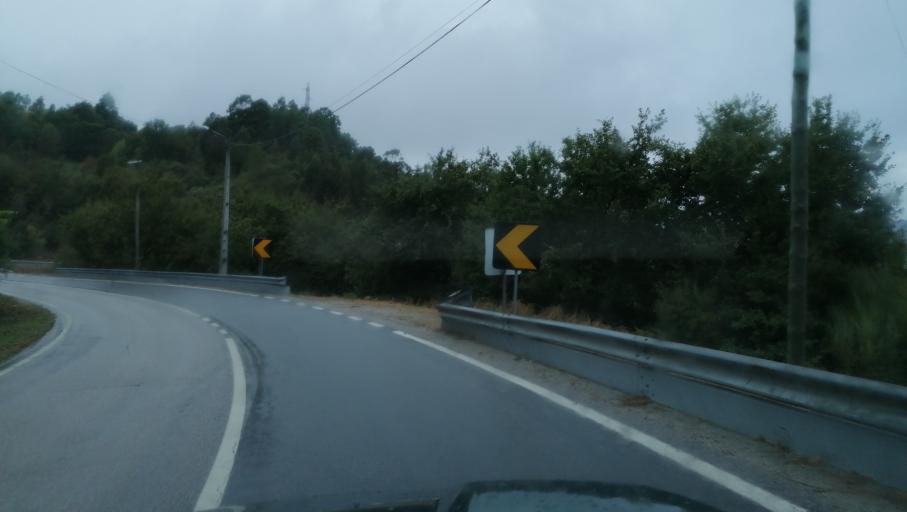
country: PT
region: Vila Real
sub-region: Ribeira de Pena
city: Ribeira de Pena
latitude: 41.5172
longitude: -7.8209
